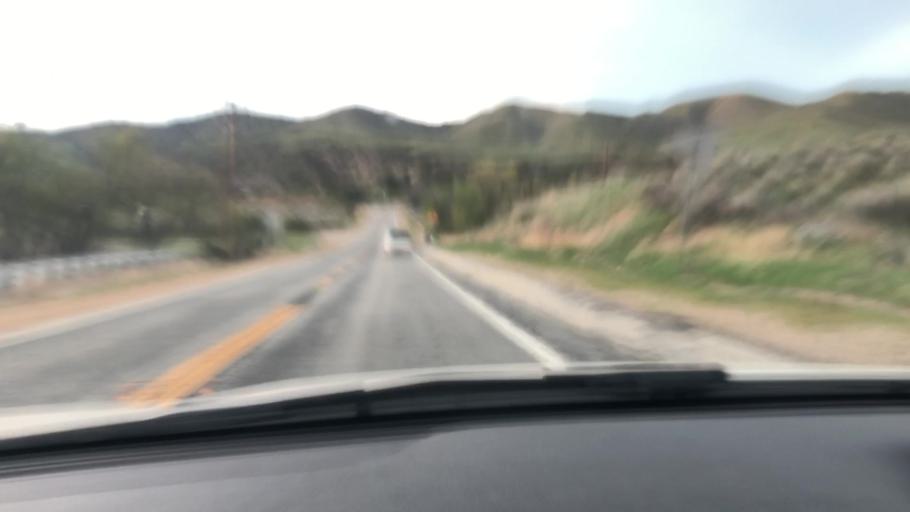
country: US
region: California
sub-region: Los Angeles County
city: Leona Valley
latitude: 34.6083
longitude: -118.2717
